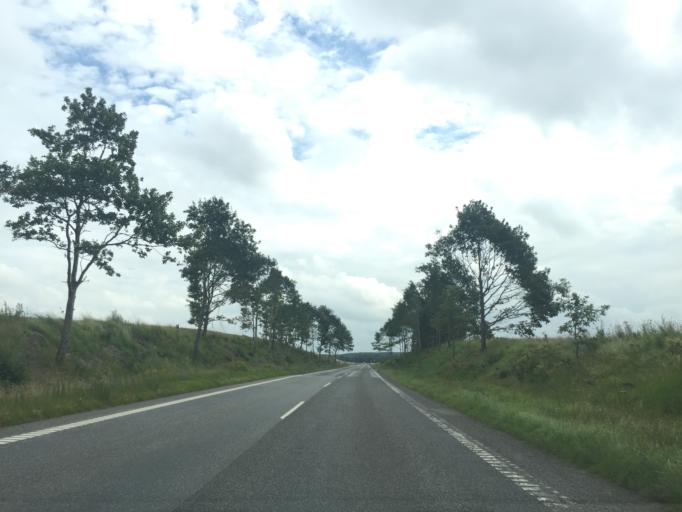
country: DK
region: Central Jutland
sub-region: Favrskov Kommune
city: Ulstrup
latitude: 56.3178
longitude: 9.7856
